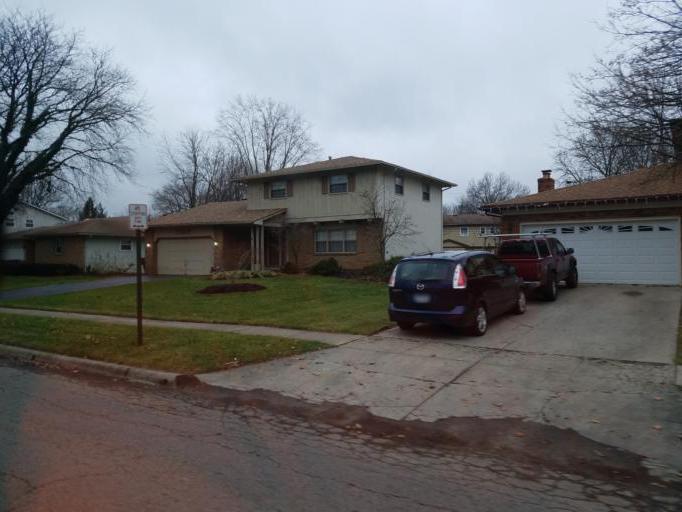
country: US
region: Ohio
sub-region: Franklin County
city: Minerva Park
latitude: 40.0783
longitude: -82.9685
